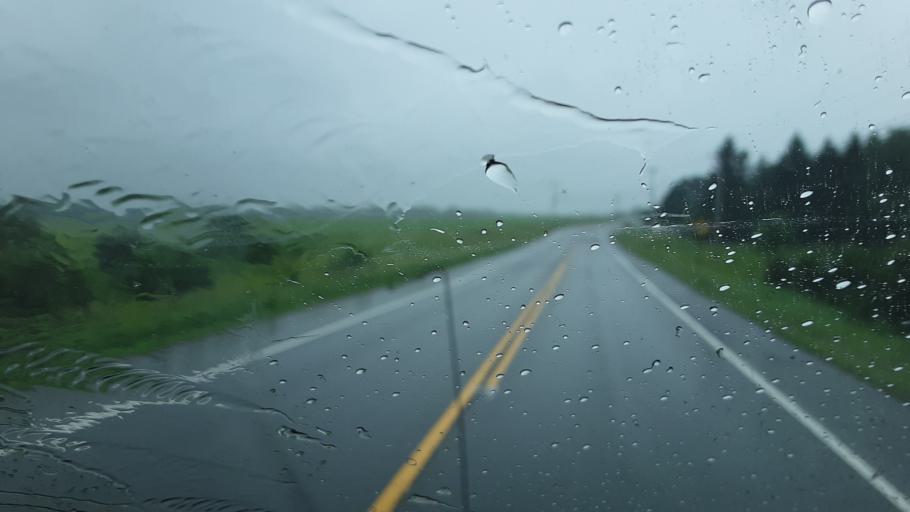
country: US
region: Maine
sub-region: Aroostook County
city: Presque Isle
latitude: 46.5902
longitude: -68.3850
